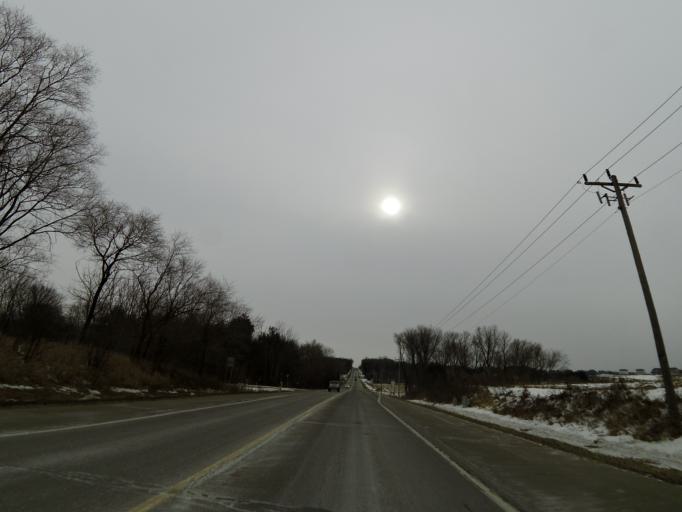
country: US
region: Minnesota
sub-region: Washington County
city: Lake Elmo
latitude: 44.9353
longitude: -92.8627
